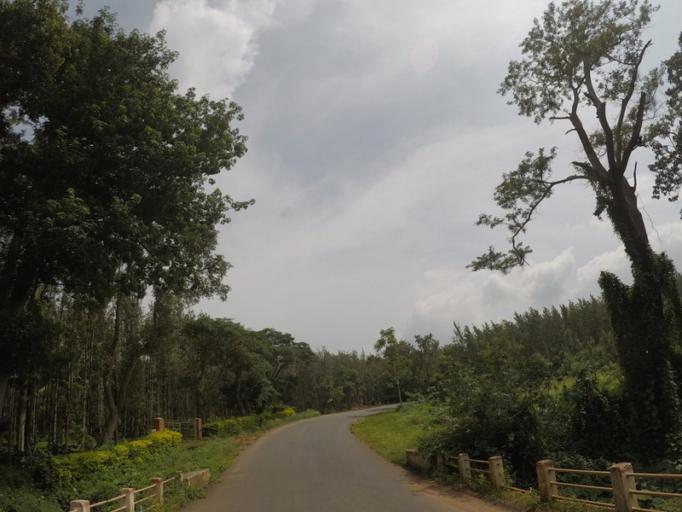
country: IN
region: Karnataka
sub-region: Chikmagalur
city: Chikmagalur
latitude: 13.4072
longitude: 75.7963
